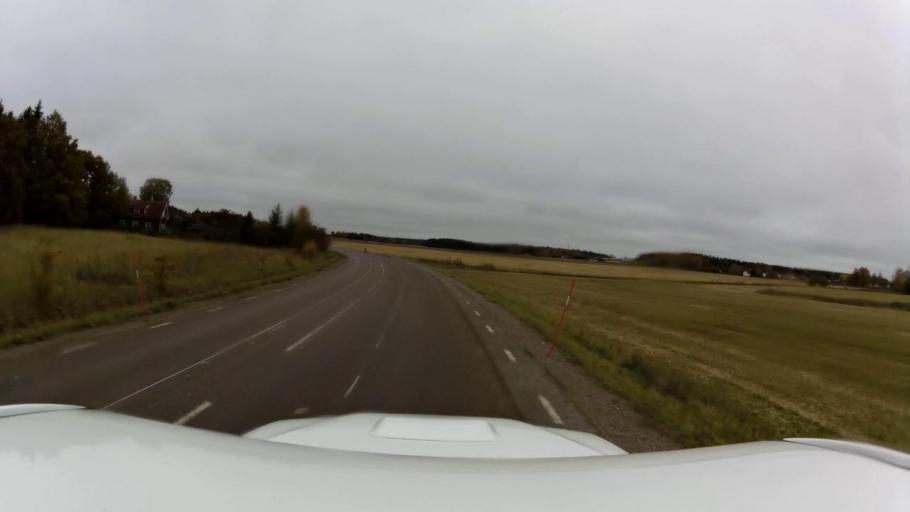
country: SE
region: OEstergoetland
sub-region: Linkopings Kommun
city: Linghem
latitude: 58.4380
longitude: 15.7147
